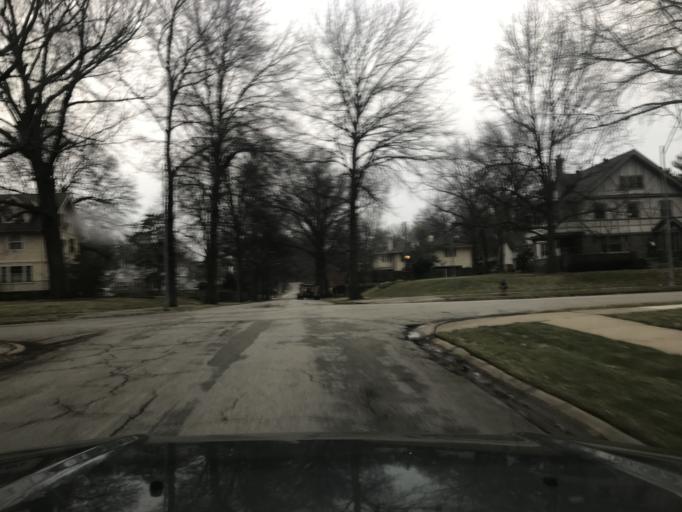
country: US
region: Kansas
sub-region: Johnson County
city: Mission Hills
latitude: 39.0270
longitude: -94.5973
